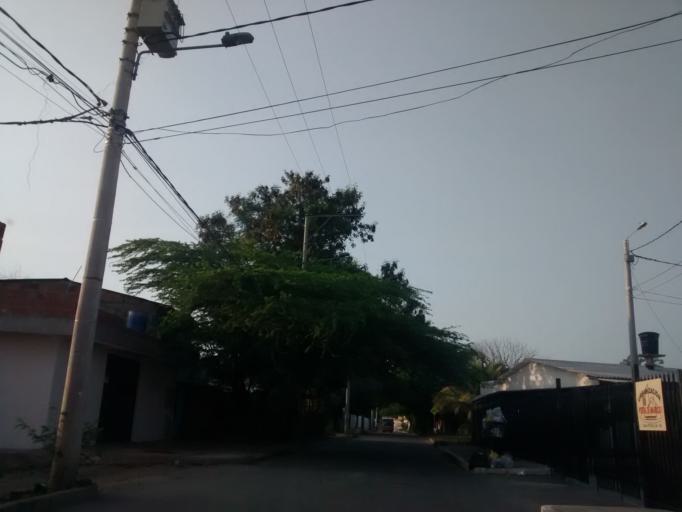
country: CO
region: Cundinamarca
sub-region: Girardot
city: Girardot City
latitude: 4.3183
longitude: -74.7839
